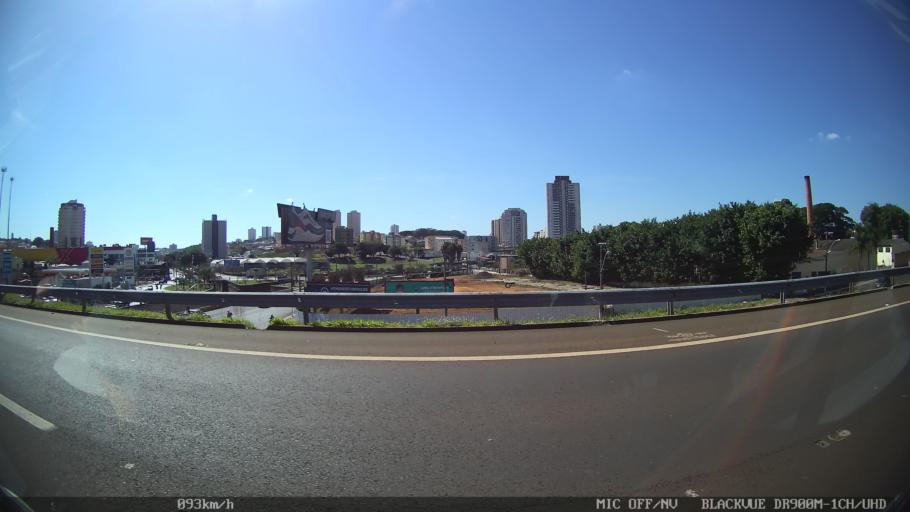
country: BR
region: Sao Paulo
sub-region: Franca
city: Franca
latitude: -20.5538
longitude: -47.4098
